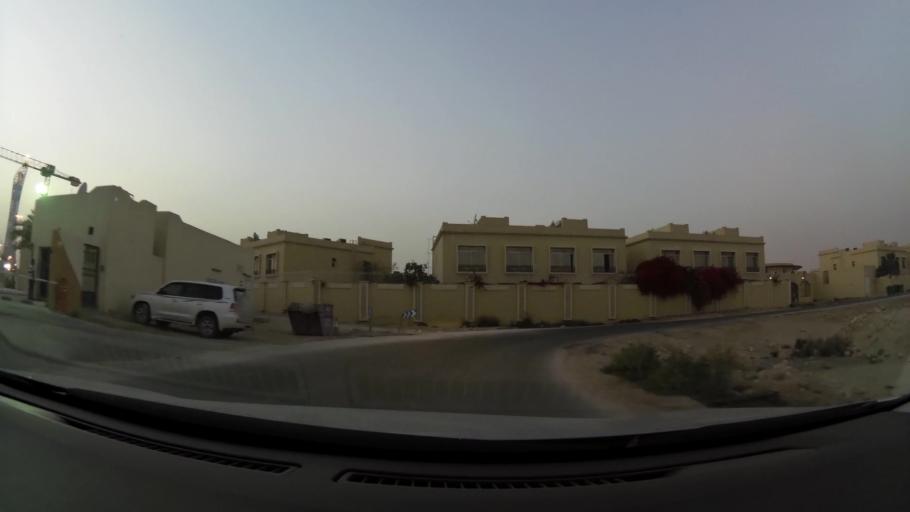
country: QA
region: Baladiyat ar Rayyan
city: Ar Rayyan
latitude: 25.2602
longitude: 51.4563
